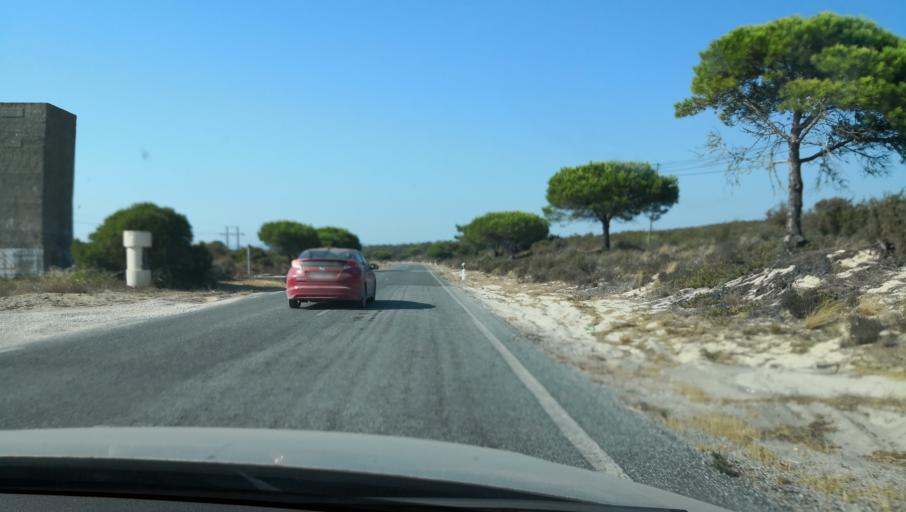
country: PT
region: Setubal
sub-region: Setubal
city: Setubal
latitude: 38.4372
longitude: -8.8315
